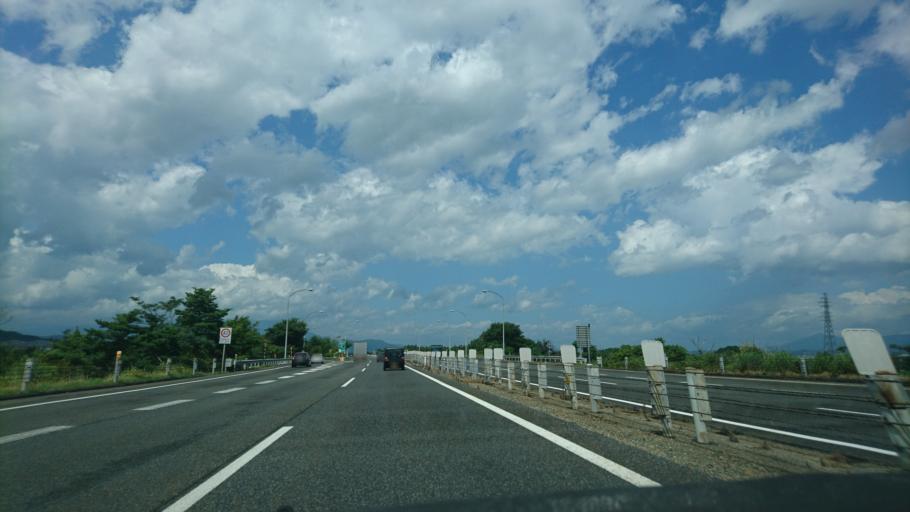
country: JP
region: Iwate
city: Morioka-shi
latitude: 39.6488
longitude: 141.1240
